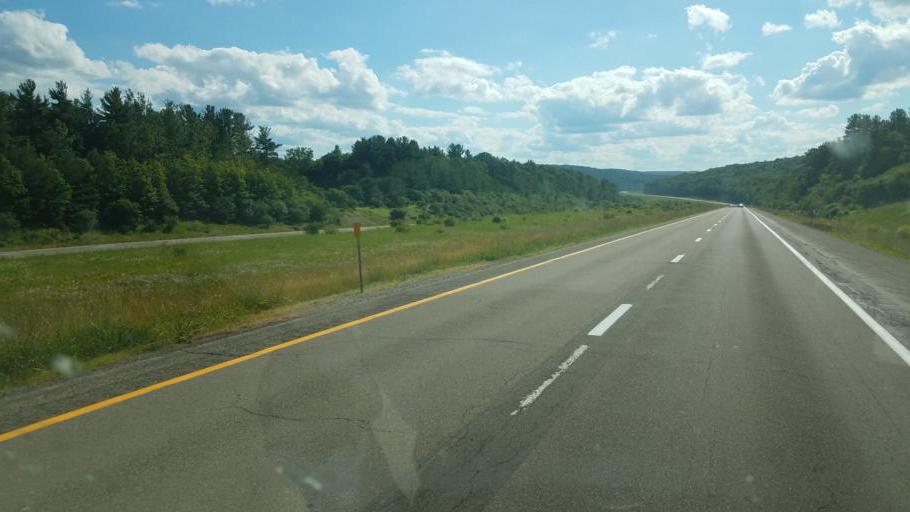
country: US
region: New York
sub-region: Allegany County
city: Alfred
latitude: 42.3029
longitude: -77.9110
